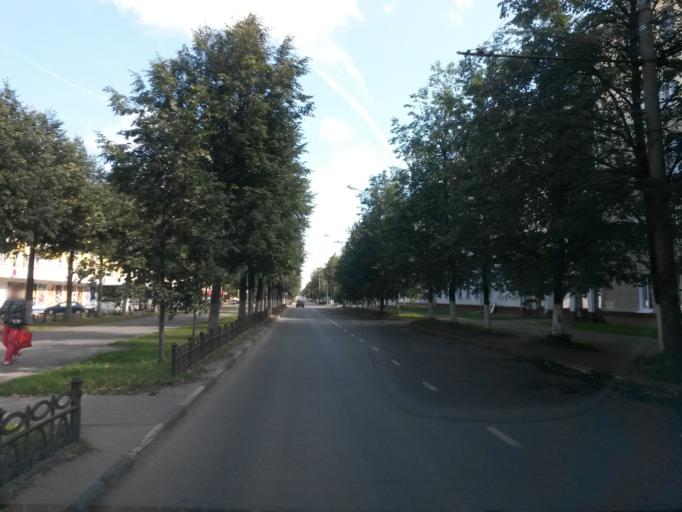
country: RU
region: Jaroslavl
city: Yaroslavl
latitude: 57.6298
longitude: 39.8506
